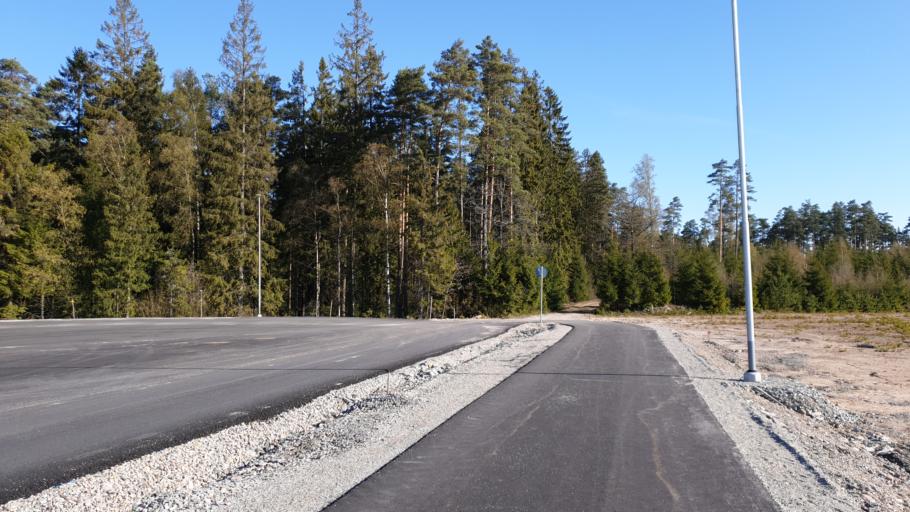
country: SE
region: Kronoberg
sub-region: Ljungby Kommun
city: Ljungby
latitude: 56.8299
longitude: 13.9016
